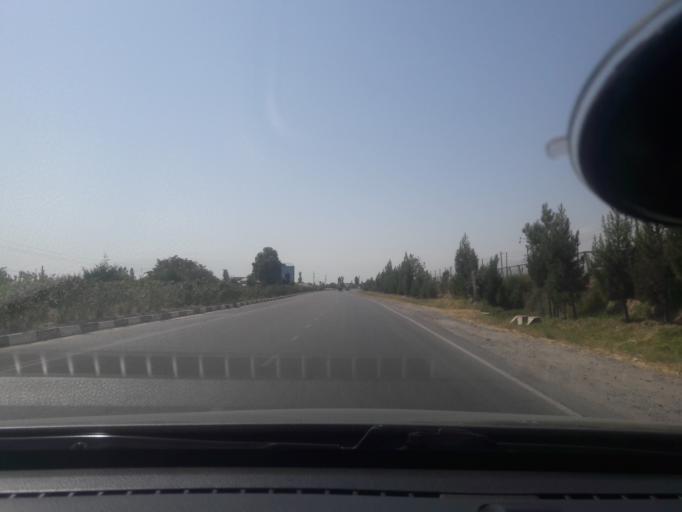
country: TJ
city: Shahrinav
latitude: 38.5614
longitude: 68.4312
